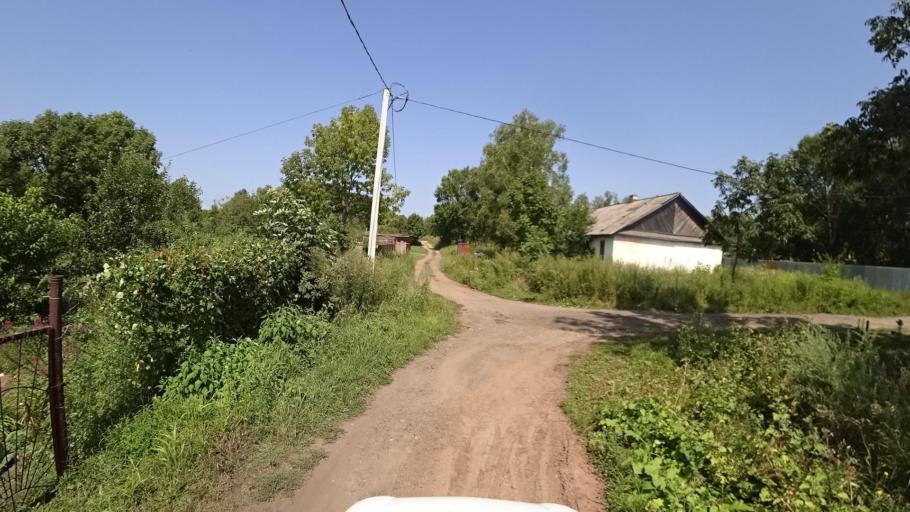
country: RU
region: Khabarovsk Krai
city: Khor
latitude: 47.9627
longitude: 135.1145
